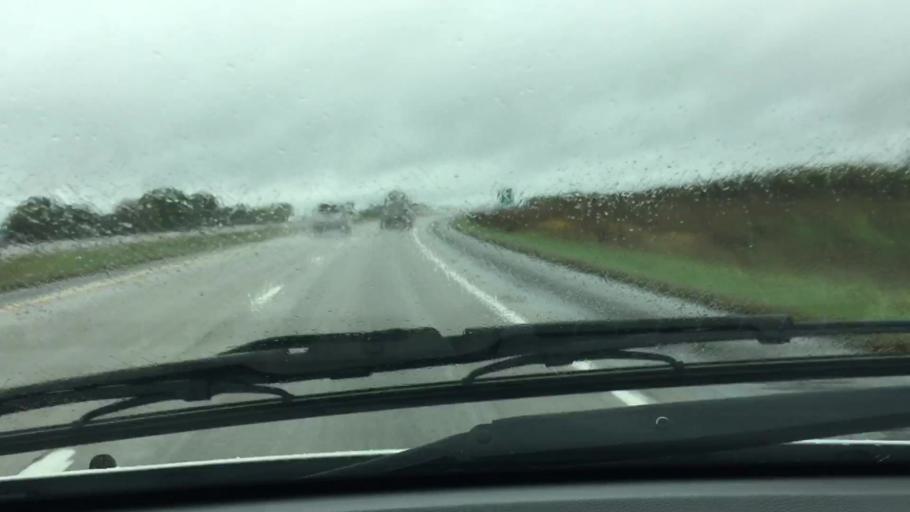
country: US
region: Iowa
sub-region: Jasper County
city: Newton
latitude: 41.6834
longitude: -92.8934
